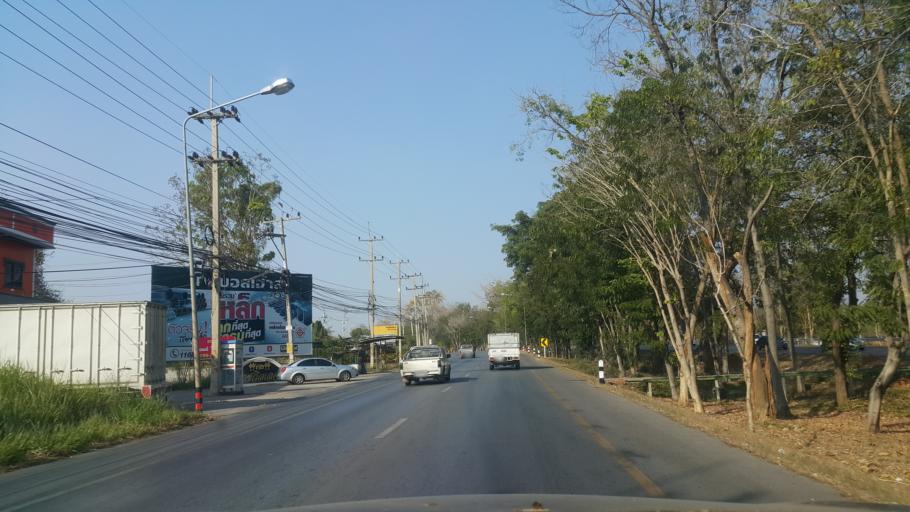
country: TH
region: Nakhon Ratchasima
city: Nakhon Ratchasima
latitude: 14.8676
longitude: 102.0718
